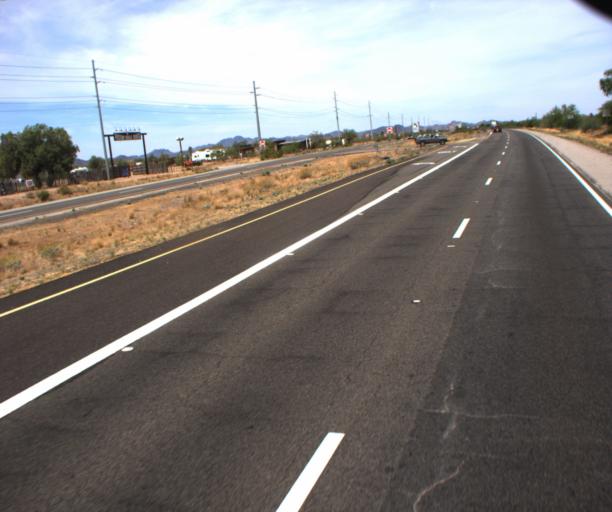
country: US
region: Arizona
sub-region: Maricopa County
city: Wickenburg
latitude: 33.8273
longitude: -112.5919
